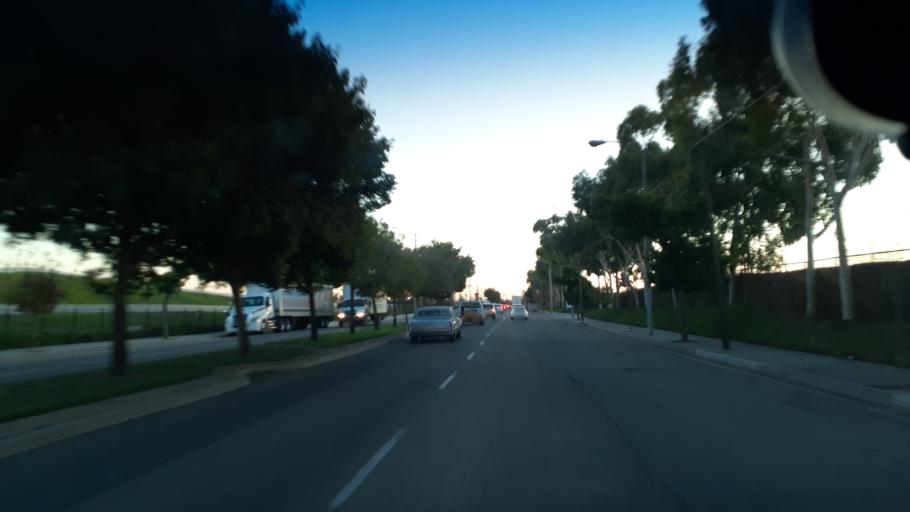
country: US
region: California
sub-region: Los Angeles County
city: Carson
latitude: 33.8497
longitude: -118.2805
